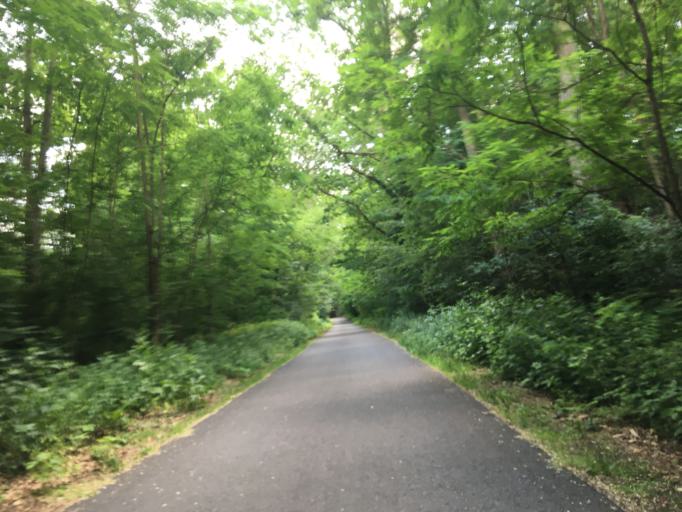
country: DE
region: Brandenburg
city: Waldsieversdorf
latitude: 52.5409
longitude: 14.0857
